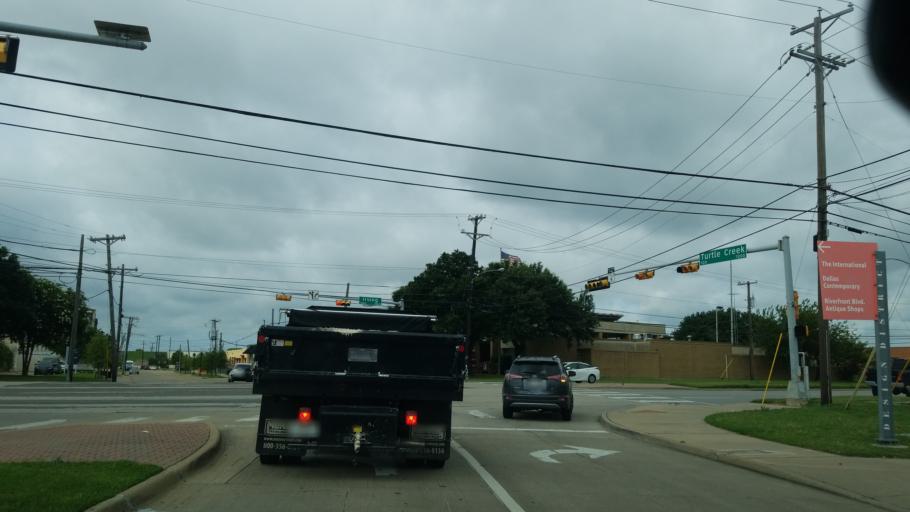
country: US
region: Texas
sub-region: Dallas County
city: Dallas
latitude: 32.7943
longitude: -96.8262
